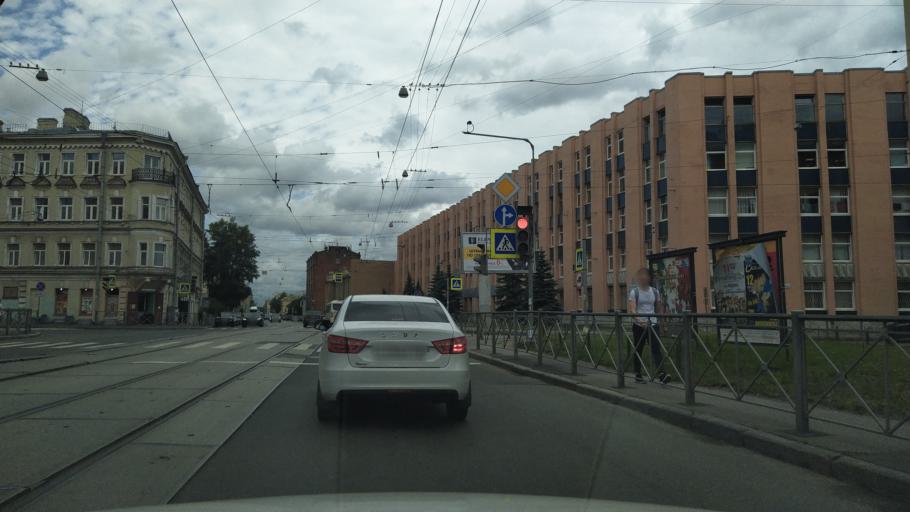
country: RU
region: Leningrad
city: Finlyandskiy
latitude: 59.9621
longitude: 30.3789
